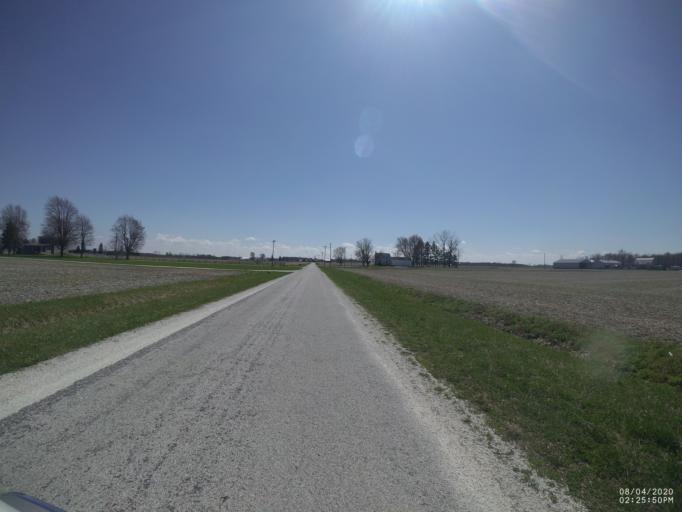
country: US
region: Ohio
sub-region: Sandusky County
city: Gibsonburg
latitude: 41.2932
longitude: -83.2596
